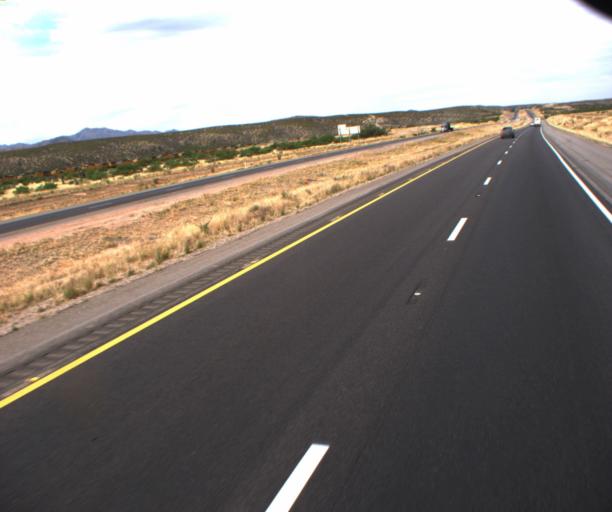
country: US
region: Arizona
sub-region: Cochise County
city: Mescal
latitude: 31.9847
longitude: -110.5566
